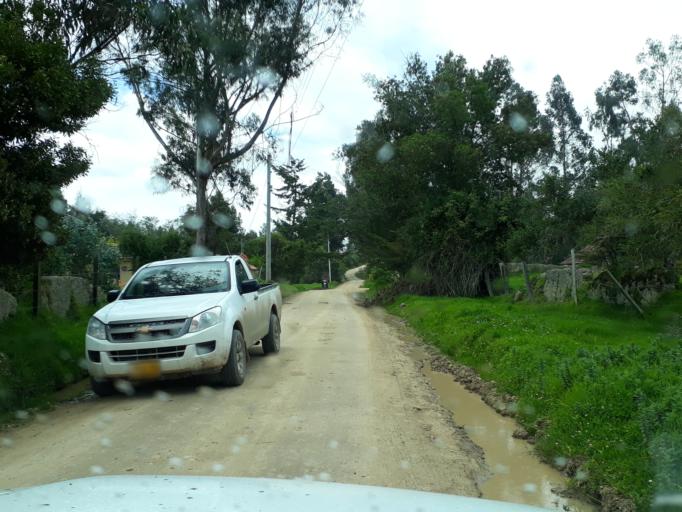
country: CO
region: Cundinamarca
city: Guasca
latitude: 4.8584
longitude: -73.8888
